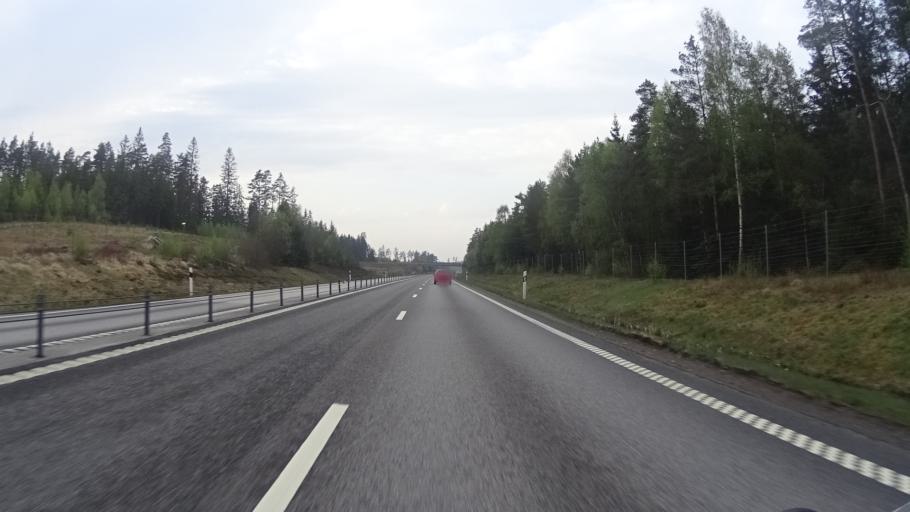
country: SE
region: Kronoberg
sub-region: Ljungby Kommun
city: Ljungby
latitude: 56.7783
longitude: 13.8822
